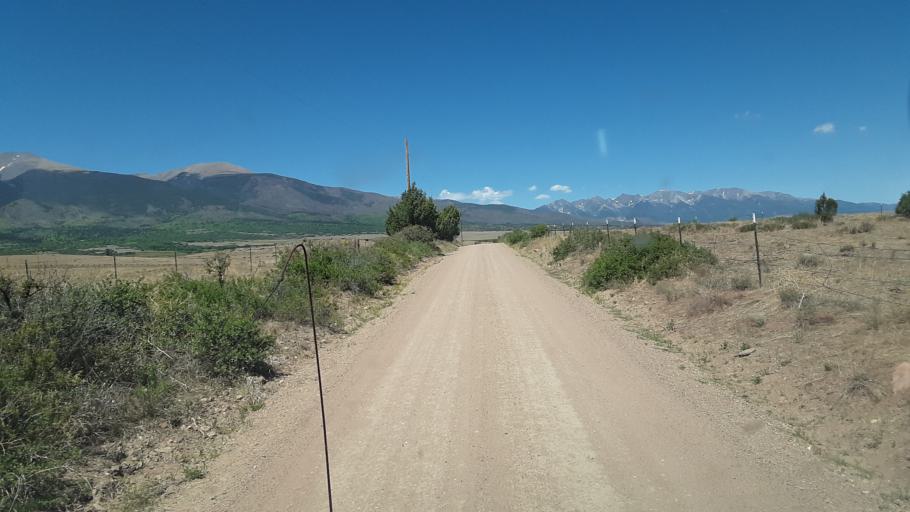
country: US
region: Colorado
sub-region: Custer County
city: Westcliffe
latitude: 38.2835
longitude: -105.6092
